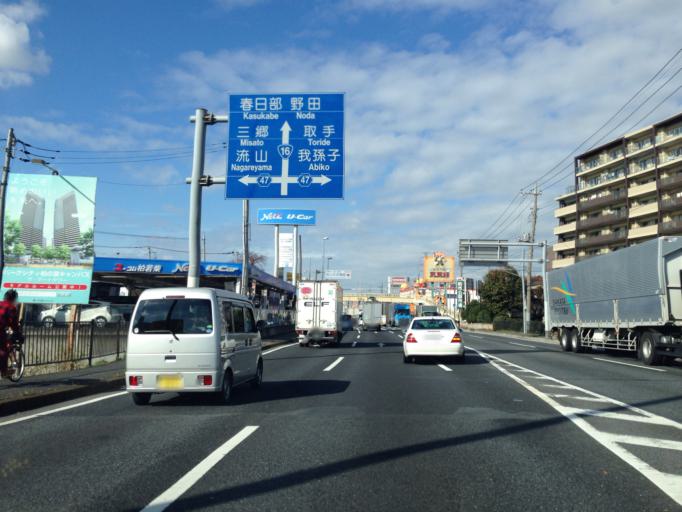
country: JP
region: Chiba
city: Kashiwa
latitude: 35.8908
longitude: 139.9603
